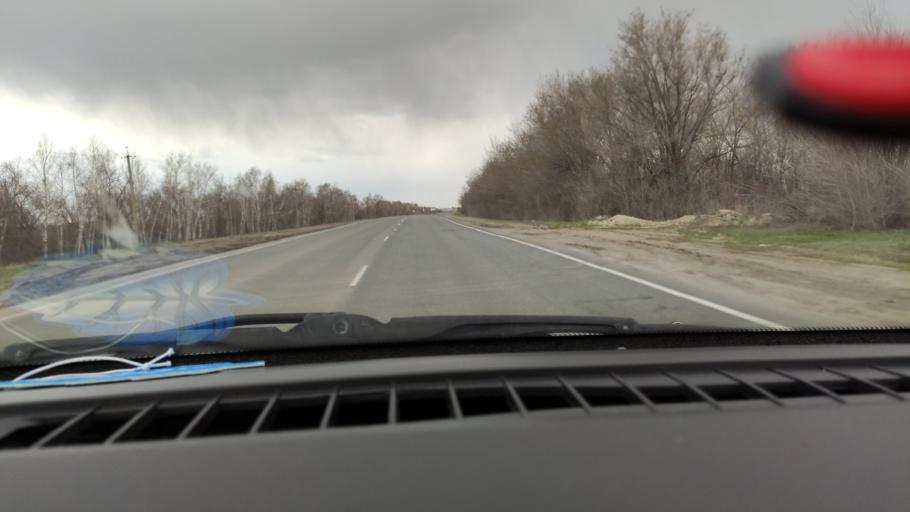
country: RU
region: Saratov
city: Sinodskoye
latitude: 52.0241
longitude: 46.7117
